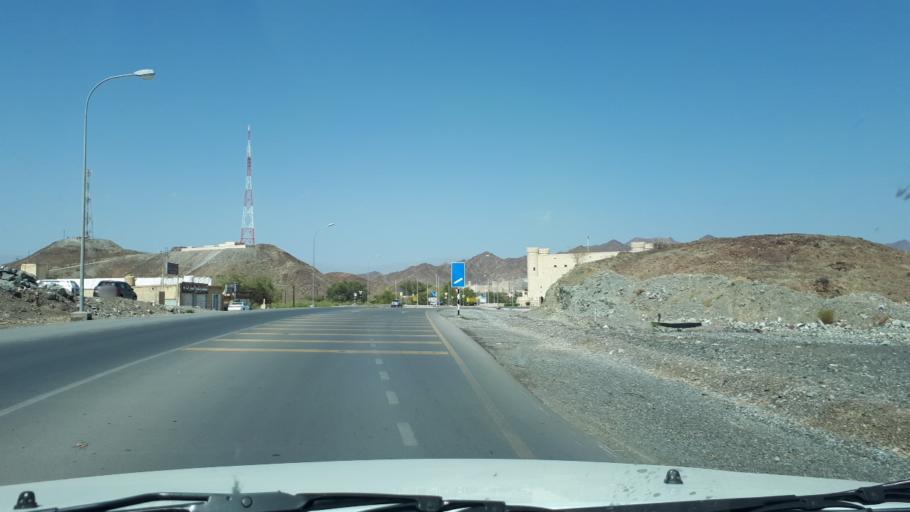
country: OM
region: Muhafazat ad Dakhiliyah
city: Bahla'
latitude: 22.9584
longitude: 57.2891
